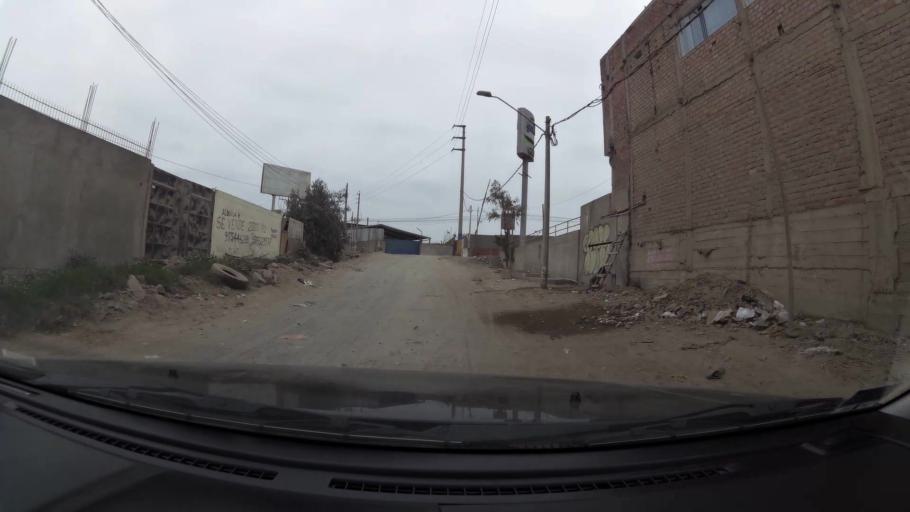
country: PE
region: Lima
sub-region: Lima
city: Surco
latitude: -12.2130
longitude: -76.9660
